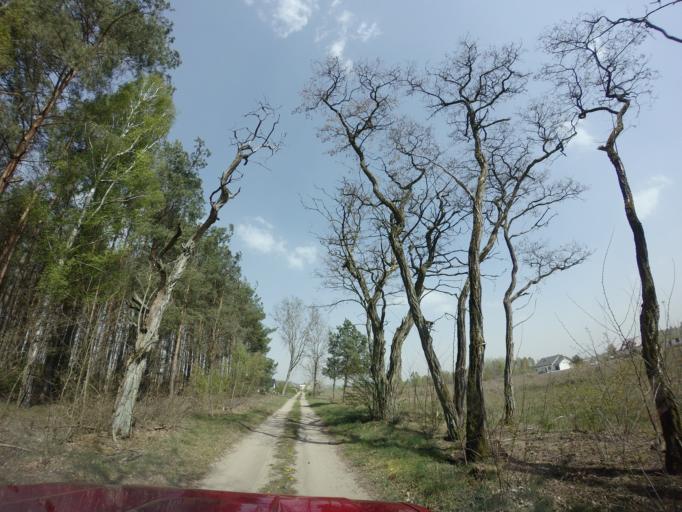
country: PL
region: West Pomeranian Voivodeship
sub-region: Powiat choszczenski
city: Drawno
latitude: 53.2143
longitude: 15.7355
